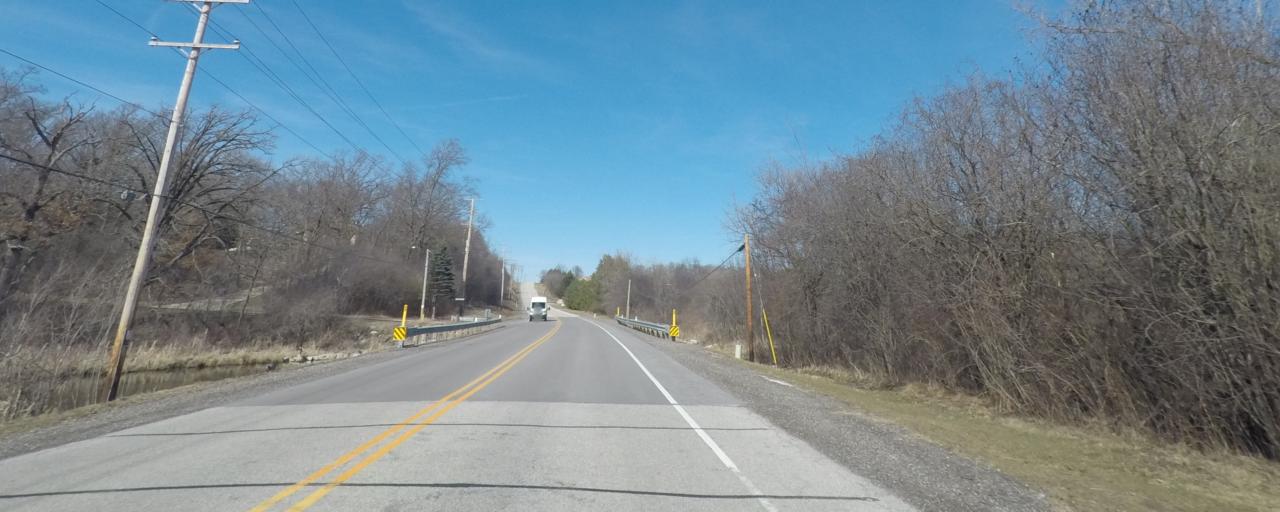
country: US
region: Wisconsin
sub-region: Waukesha County
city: Merton
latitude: 43.1479
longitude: -88.3267
